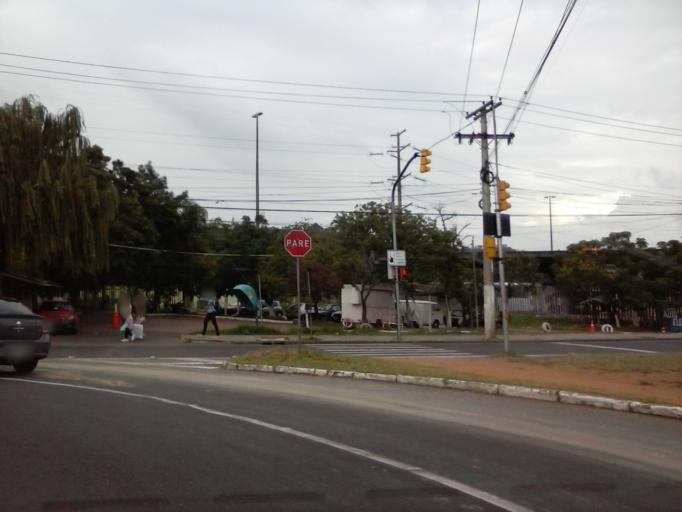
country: BR
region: Rio Grande do Sul
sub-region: Porto Alegre
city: Porto Alegre
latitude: -30.0654
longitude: -51.1510
